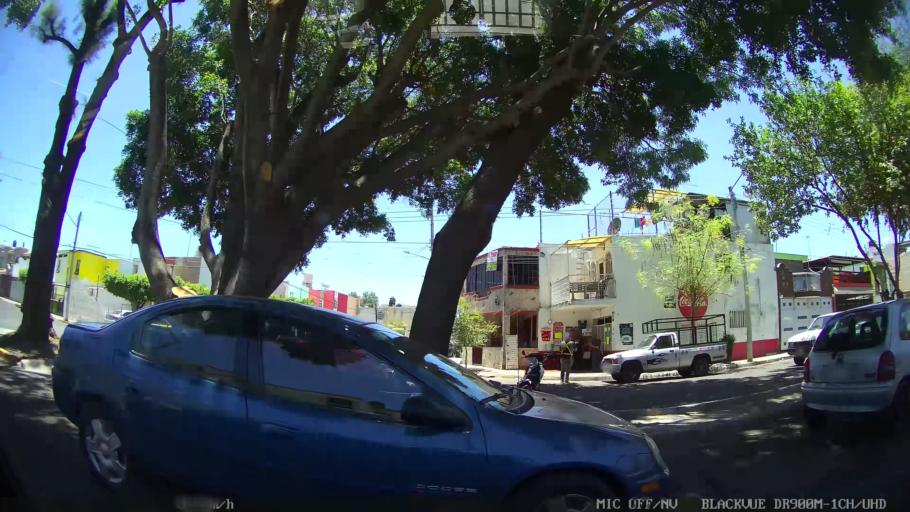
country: MX
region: Jalisco
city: Tlaquepaque
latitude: 20.6747
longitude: -103.2931
